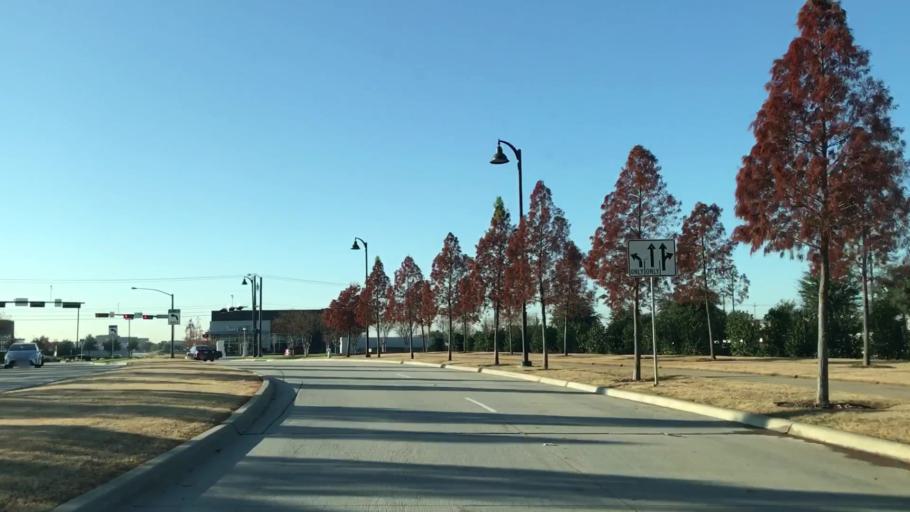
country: US
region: Texas
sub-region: Dallas County
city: Coppell
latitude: 32.9266
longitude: -96.9903
